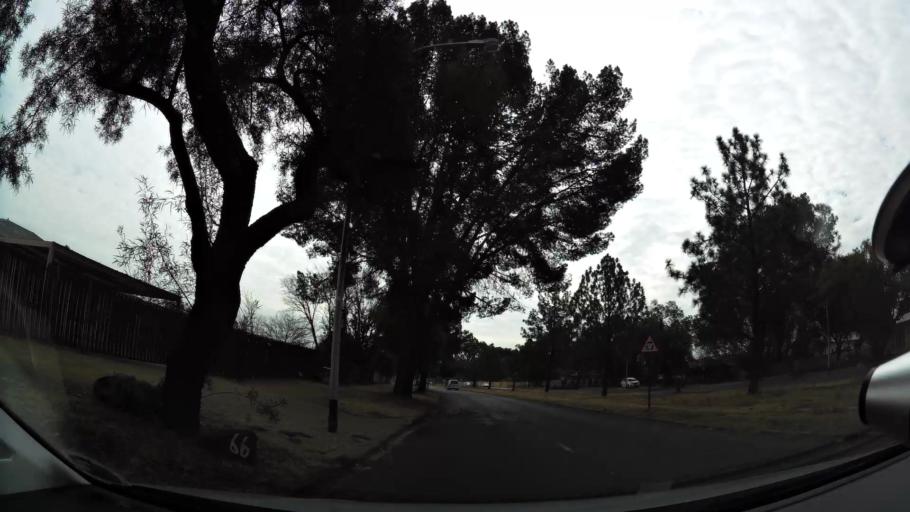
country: ZA
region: Orange Free State
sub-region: Mangaung Metropolitan Municipality
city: Bloemfontein
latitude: -29.1285
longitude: 26.2017
